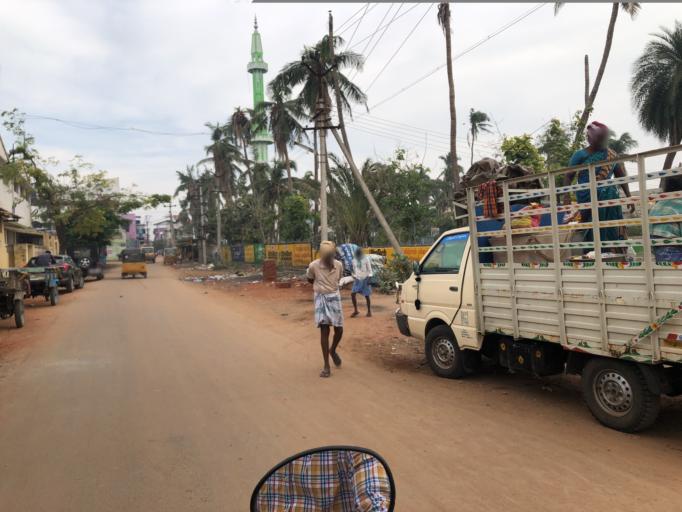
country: IN
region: Tamil Nadu
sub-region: Thanjavur
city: Adirampattinam
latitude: 10.3393
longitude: 79.3798
